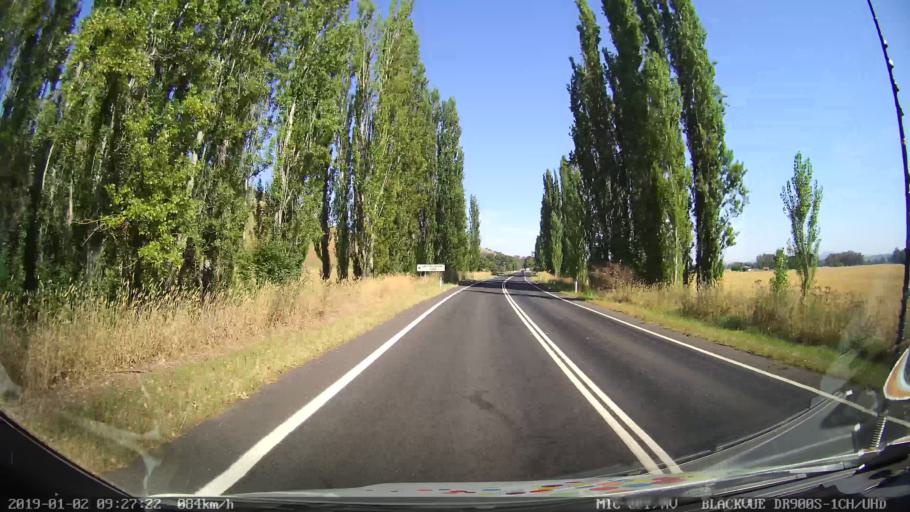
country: AU
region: New South Wales
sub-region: Tumut Shire
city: Tumut
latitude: -35.3625
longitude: 148.2585
